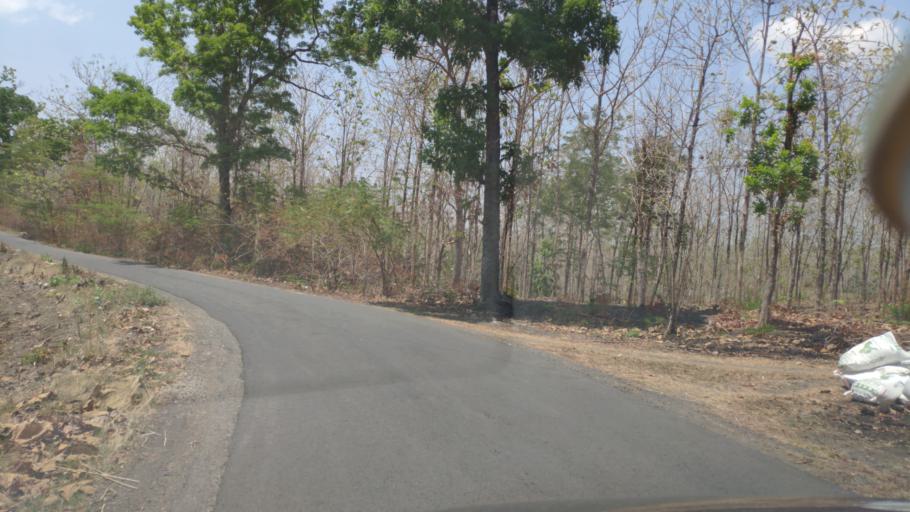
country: ID
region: Central Java
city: Randublatung
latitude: -7.2288
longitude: 111.3797
